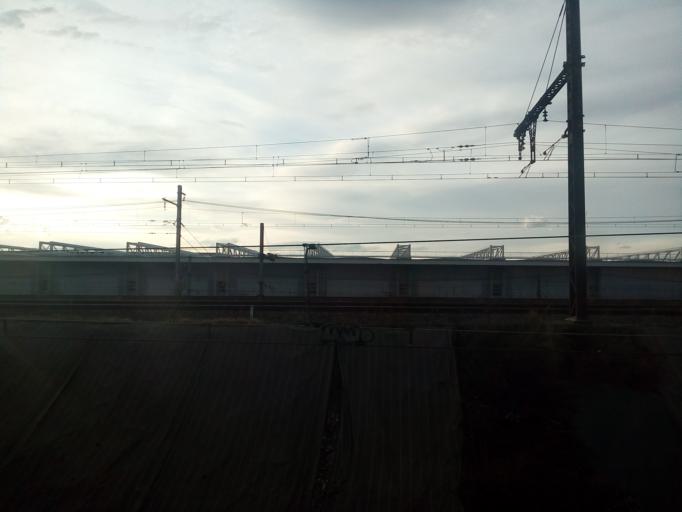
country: FR
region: Rhone-Alpes
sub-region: Departement du Rhone
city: Lyon
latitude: 45.7336
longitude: 4.8501
